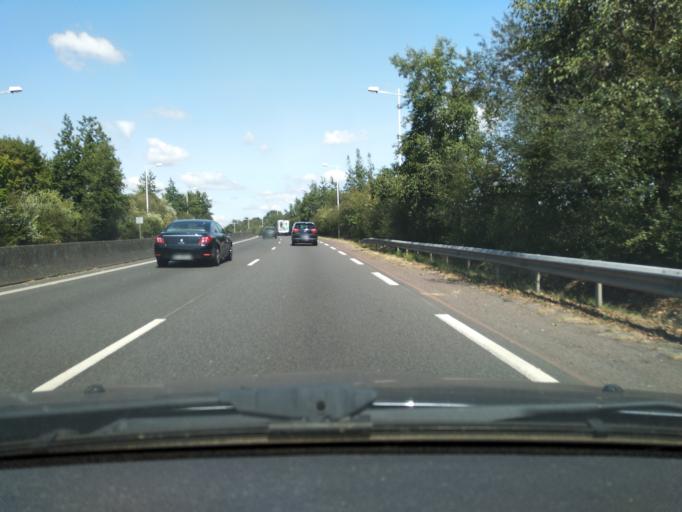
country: FR
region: Centre
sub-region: Departement d'Indre-et-Loire
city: Rochecorbon
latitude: 47.4114
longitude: 0.7207
